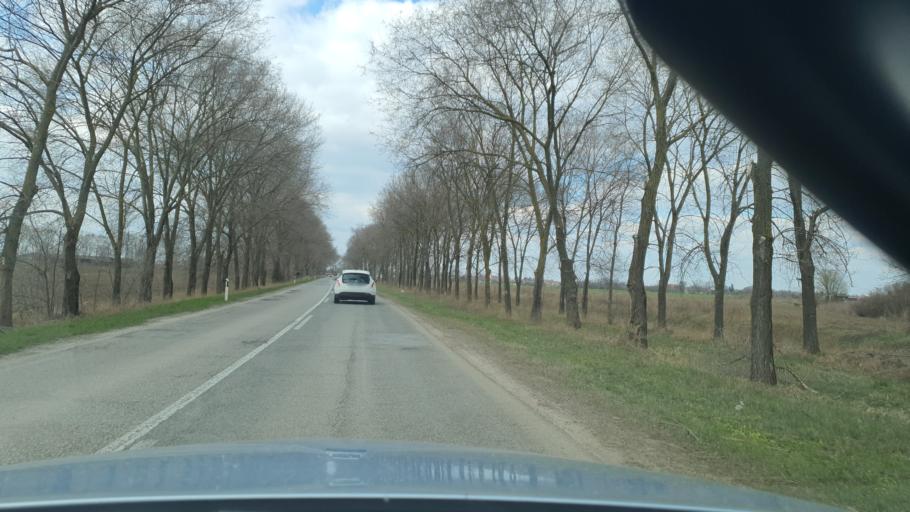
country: RS
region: Autonomna Pokrajina Vojvodina
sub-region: Zapadnobacki Okrug
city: Odzaci
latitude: 45.4476
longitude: 19.3583
